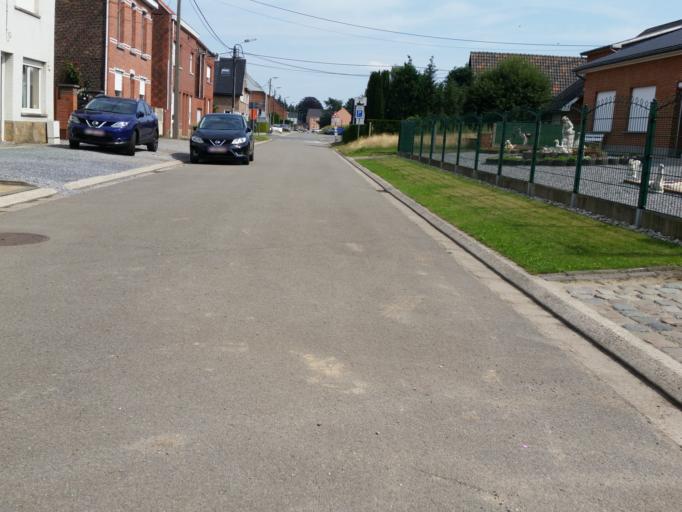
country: BE
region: Flanders
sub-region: Provincie Vlaams-Brabant
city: Zemst
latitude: 50.9606
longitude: 4.4906
